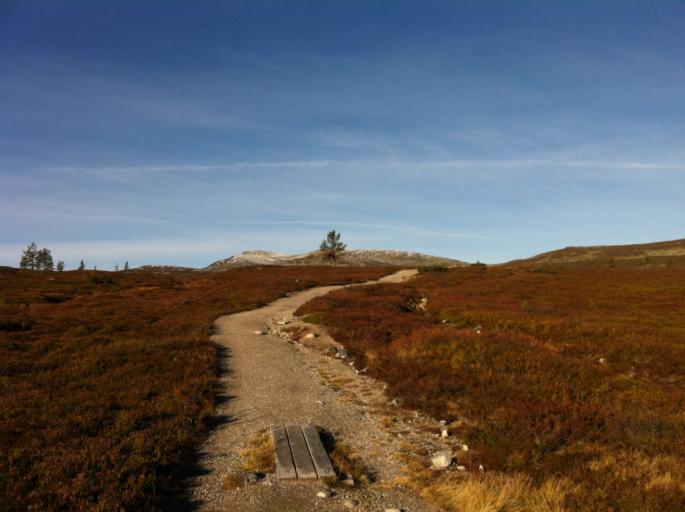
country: NO
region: Hedmark
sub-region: Engerdal
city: Engerdal
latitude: 62.1117
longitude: 12.2748
